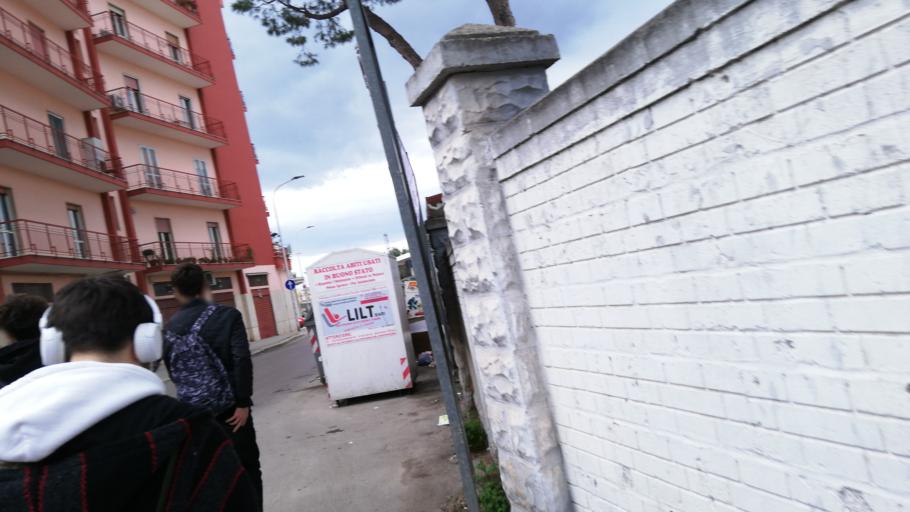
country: IT
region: Apulia
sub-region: Provincia di Bari
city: Bitonto
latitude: 41.1130
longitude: 16.6846
